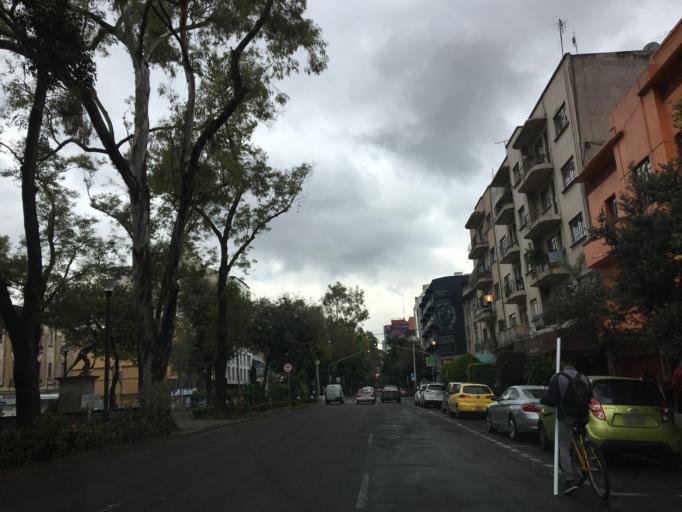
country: MX
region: Mexico City
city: Benito Juarez
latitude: 19.4193
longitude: -99.1552
